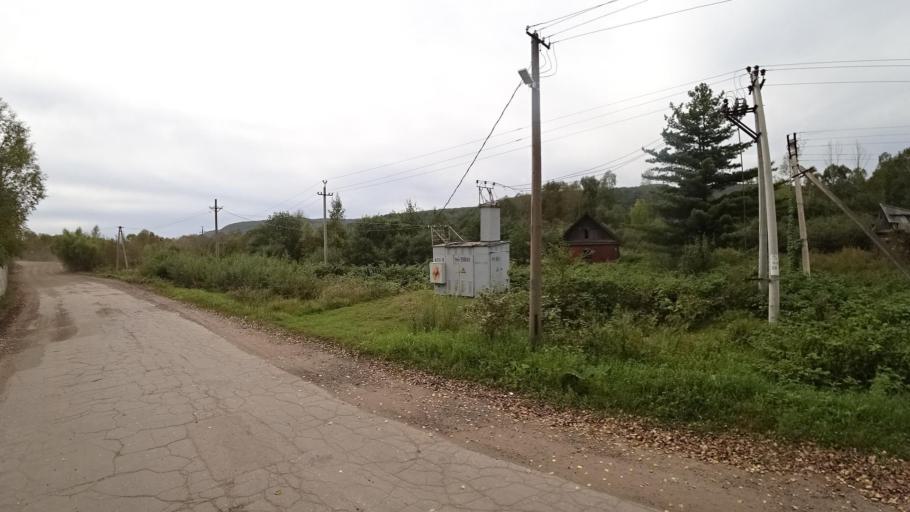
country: RU
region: Jewish Autonomous Oblast
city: Khingansk
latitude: 49.0229
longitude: 131.0541
